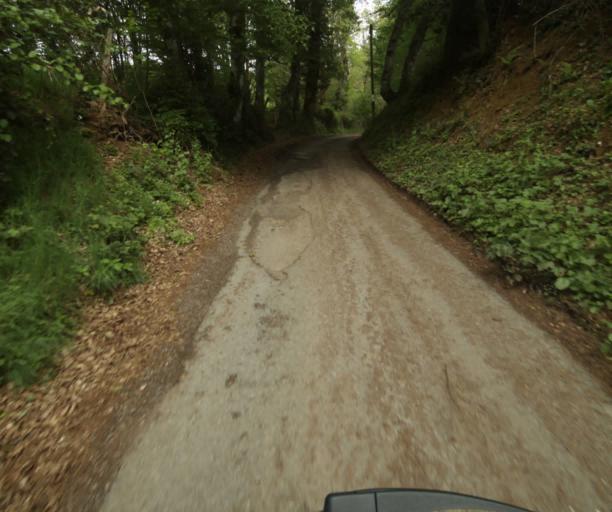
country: FR
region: Limousin
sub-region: Departement de la Correze
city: Tulle
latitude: 45.2856
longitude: 1.7773
